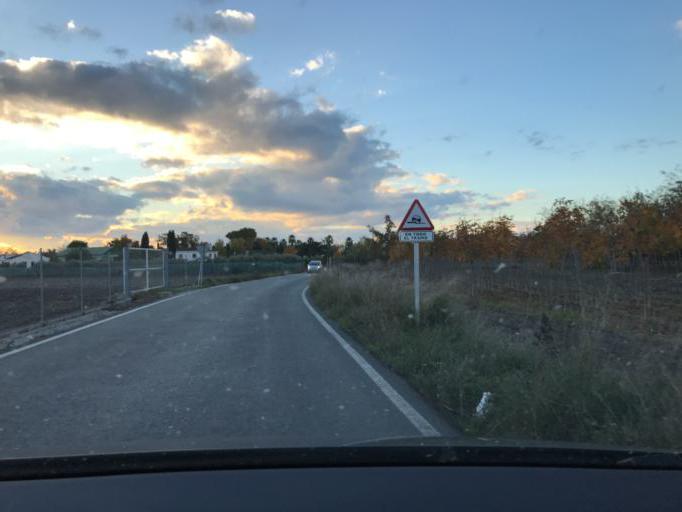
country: ES
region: Andalusia
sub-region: Provincia de Granada
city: Armilla
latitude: 37.1669
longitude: -3.6253
